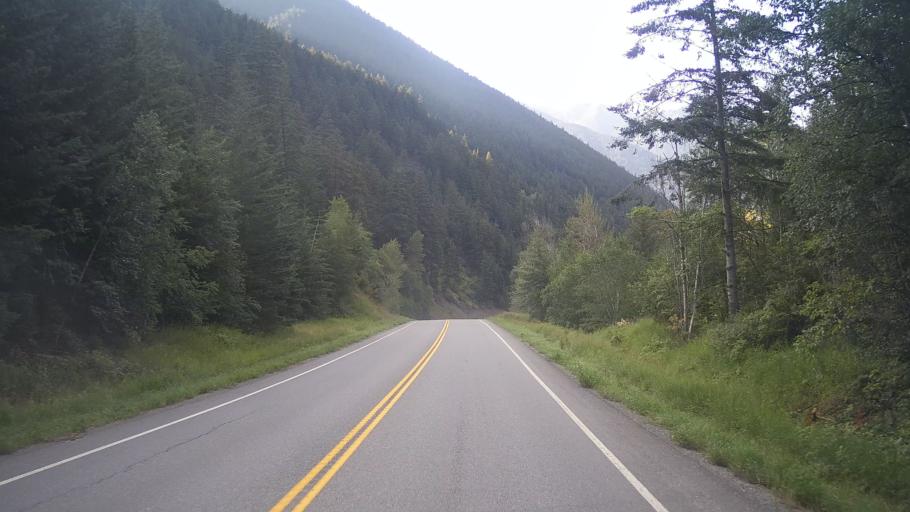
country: CA
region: British Columbia
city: Lillooet
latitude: 50.5988
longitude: -122.0973
